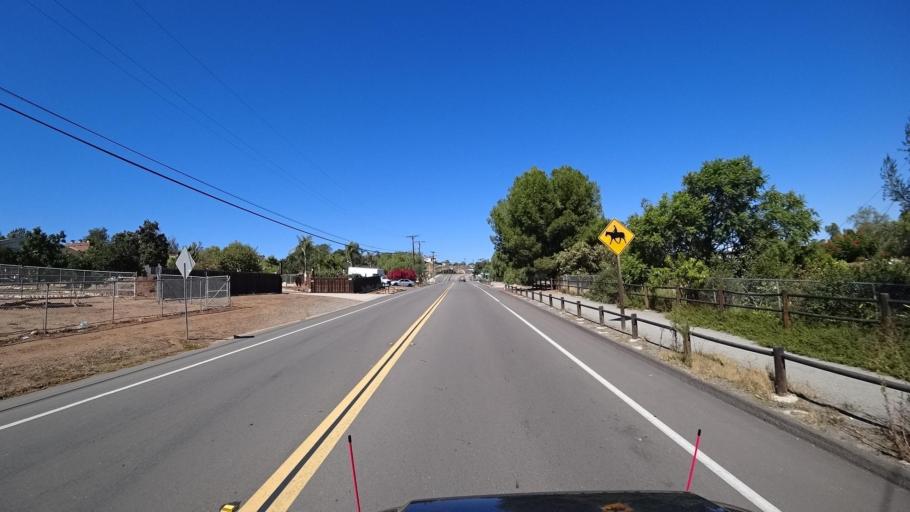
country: US
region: California
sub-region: San Diego County
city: La Presa
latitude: 32.6853
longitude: -117.0151
